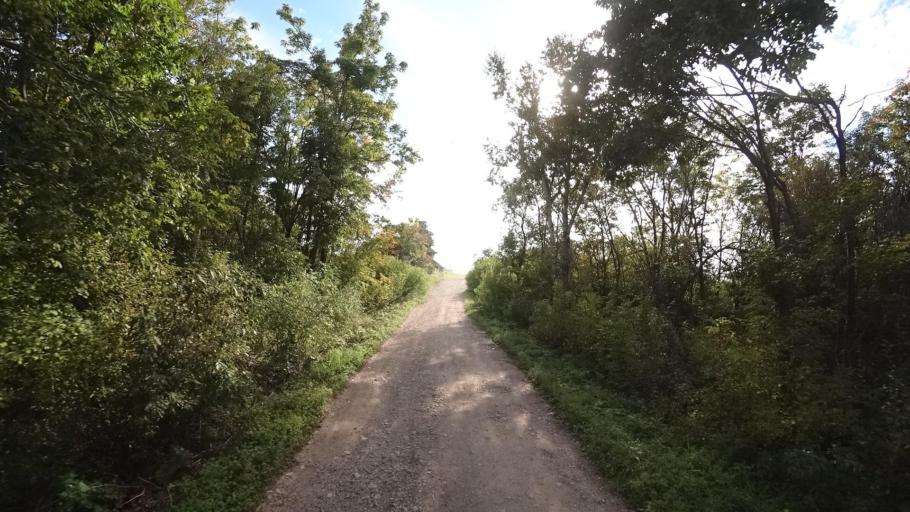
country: RU
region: Primorskiy
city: Dostoyevka
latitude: 44.2997
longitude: 133.4538
